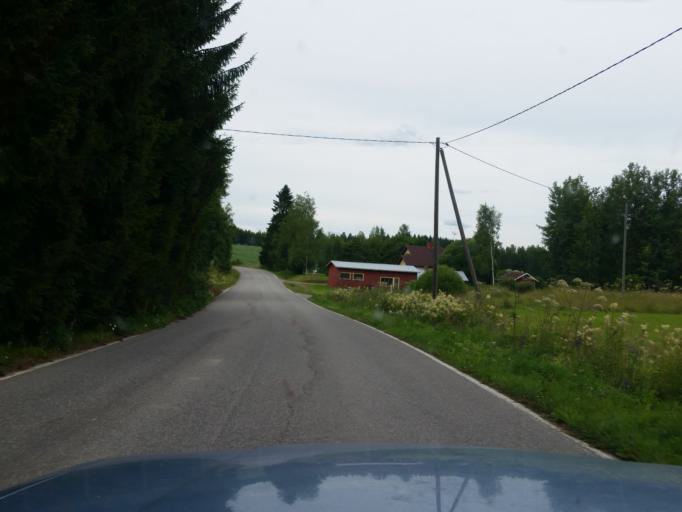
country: FI
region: Uusimaa
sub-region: Helsinki
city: Sammatti
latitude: 60.4585
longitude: 23.8483
